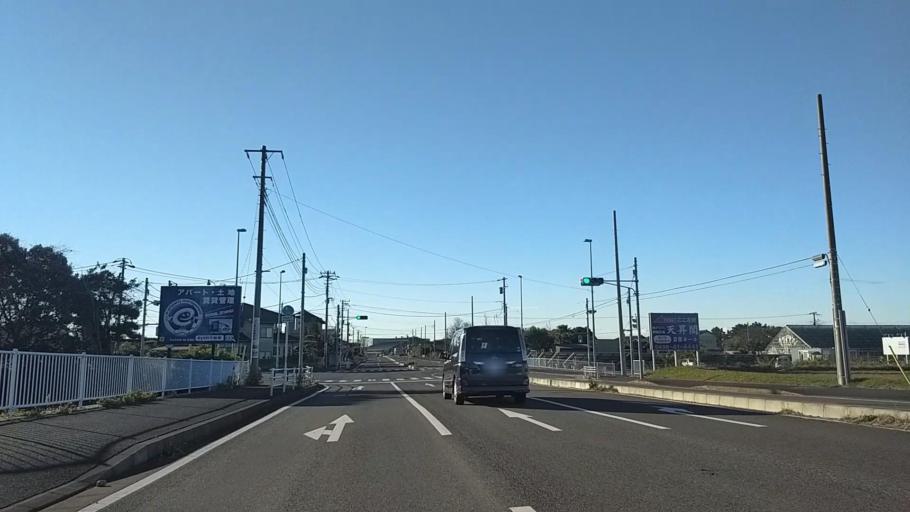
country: JP
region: Chiba
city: Kisarazu
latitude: 35.4114
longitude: 139.9185
